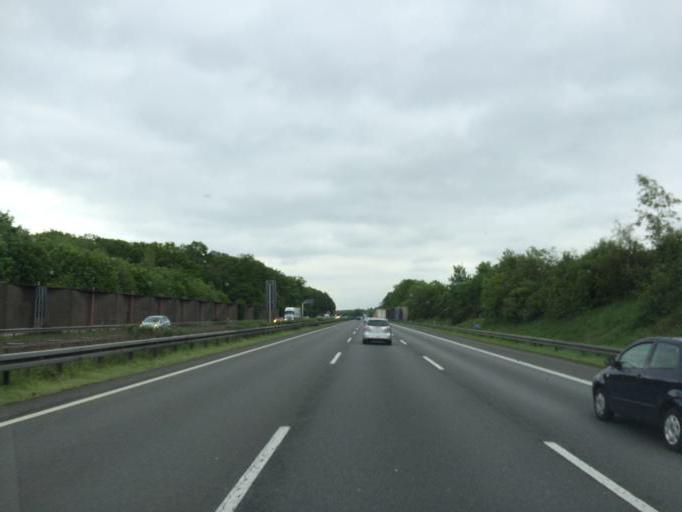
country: DE
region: Lower Saxony
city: Peine
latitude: 52.3355
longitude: 10.2810
